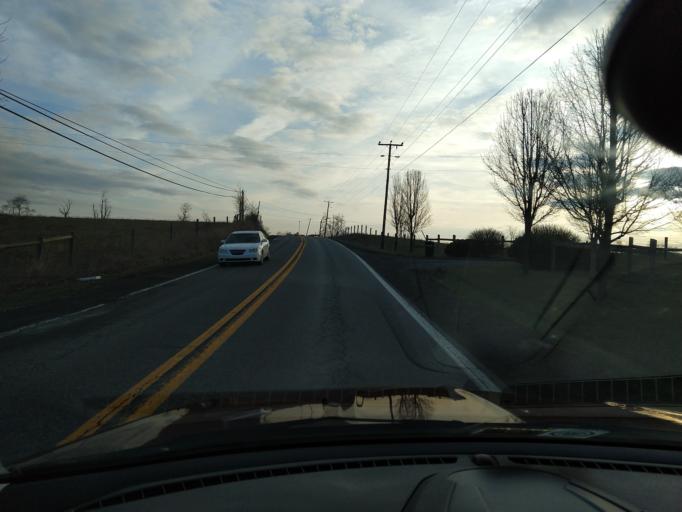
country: US
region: West Virginia
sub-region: Greenbrier County
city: Lewisburg
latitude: 37.9061
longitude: -80.3884
